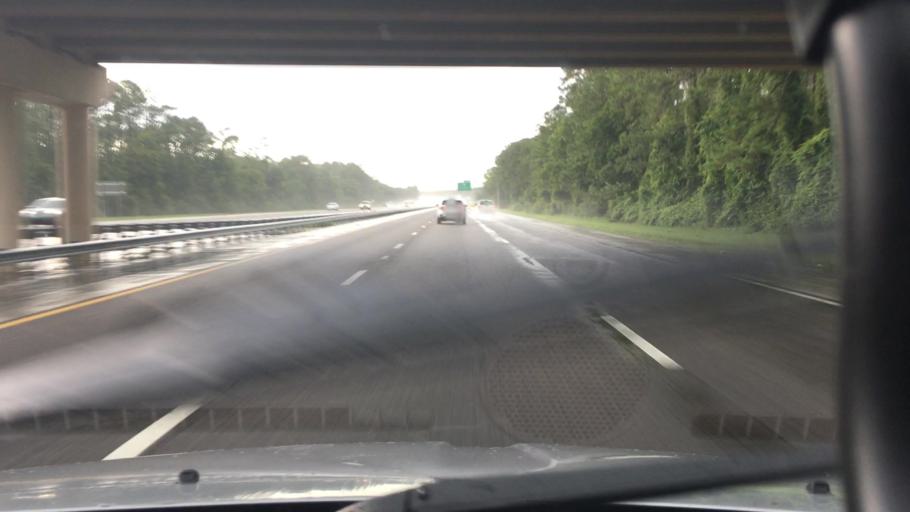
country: US
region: Florida
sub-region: Flagler County
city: Palm Coast
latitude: 29.6460
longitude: -81.2731
